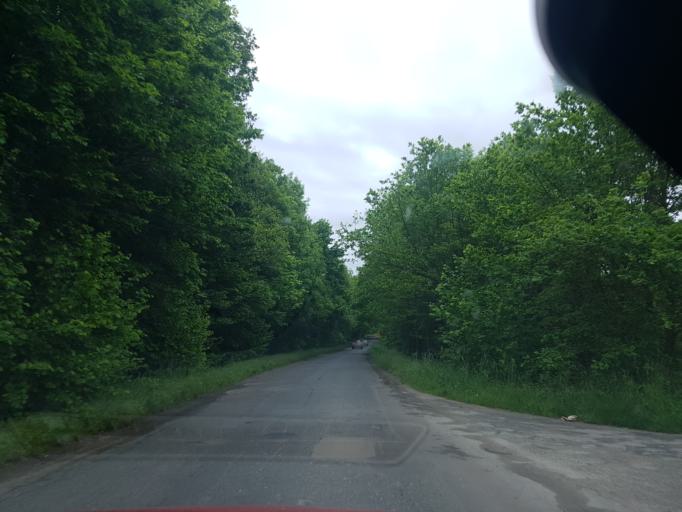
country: PL
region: Lower Silesian Voivodeship
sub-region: Powiat wroclawski
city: Katy Wroclawskie
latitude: 50.9814
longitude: 16.7632
